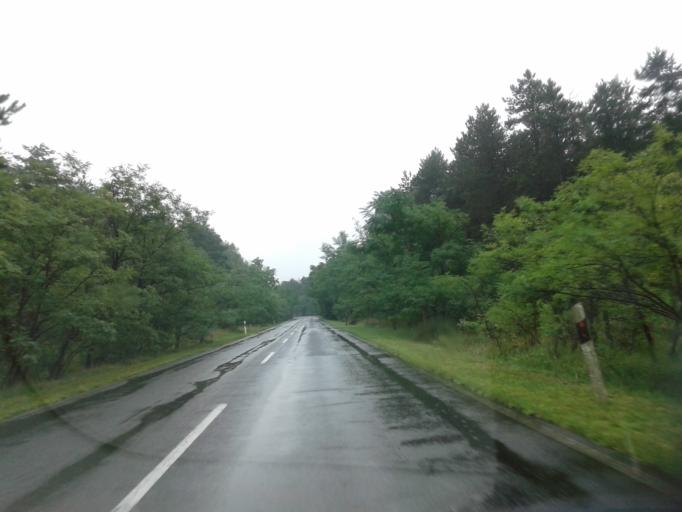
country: HU
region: Csongrad
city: Asotthalom
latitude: 46.2311
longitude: 19.7412
